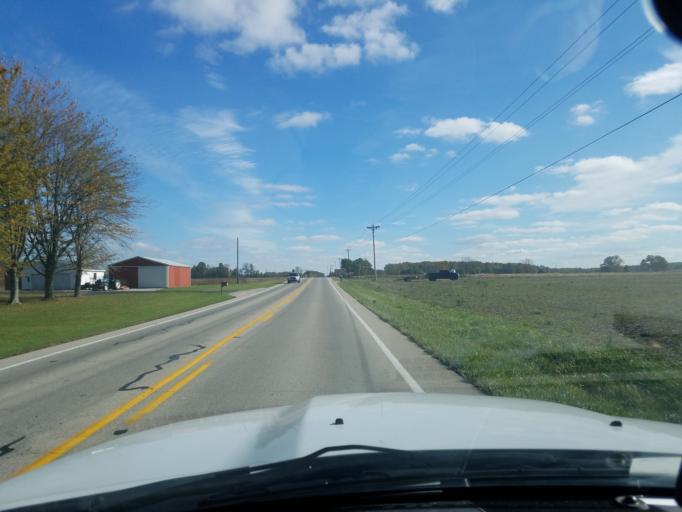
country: US
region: Indiana
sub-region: Ripley County
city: Versailles
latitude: 39.0748
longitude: -85.3060
